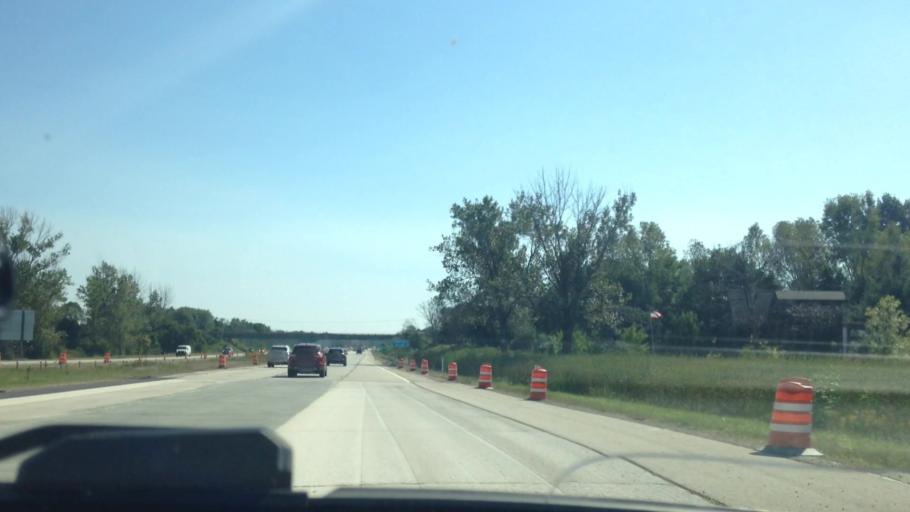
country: US
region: Wisconsin
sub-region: Ozaukee County
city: Grafton
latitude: 43.3341
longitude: -87.9238
